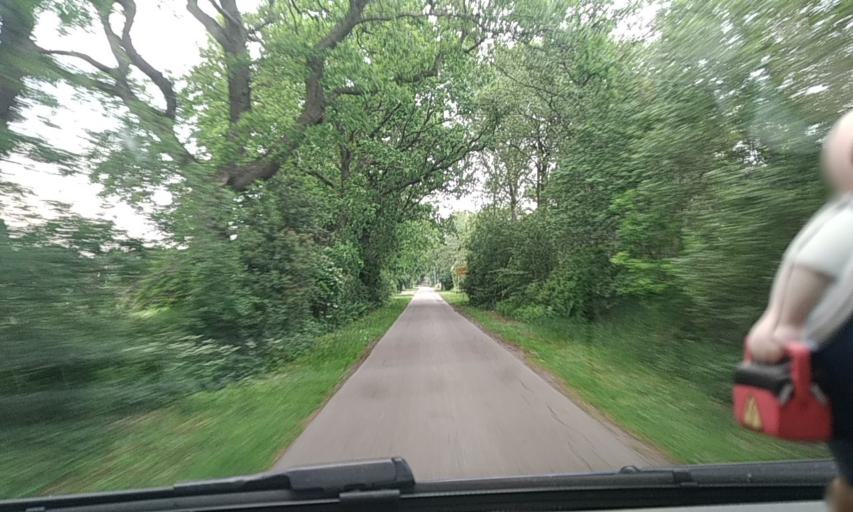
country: DE
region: Schleswig-Holstein
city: Borm
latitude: 54.3963
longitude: 9.3818
